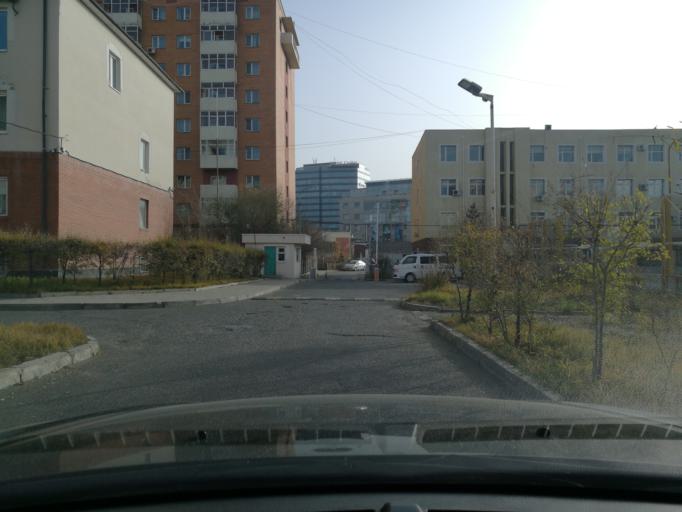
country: MN
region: Ulaanbaatar
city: Ulaanbaatar
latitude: 47.9097
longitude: 106.9106
